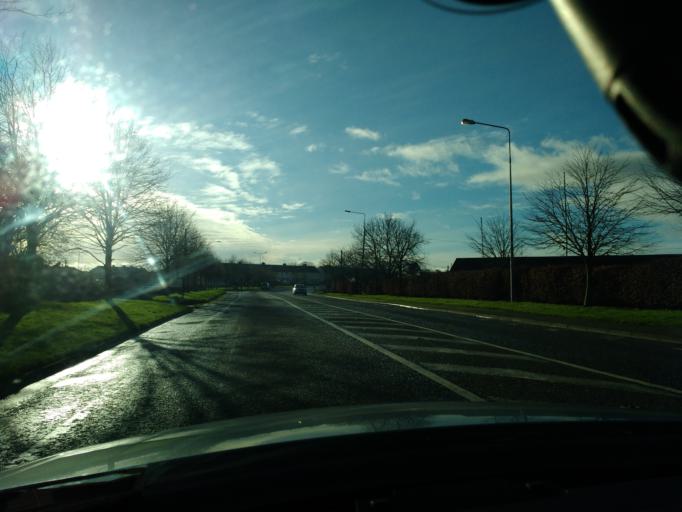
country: IE
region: Leinster
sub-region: Laois
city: Rathdowney
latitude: 52.7245
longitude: -7.5755
